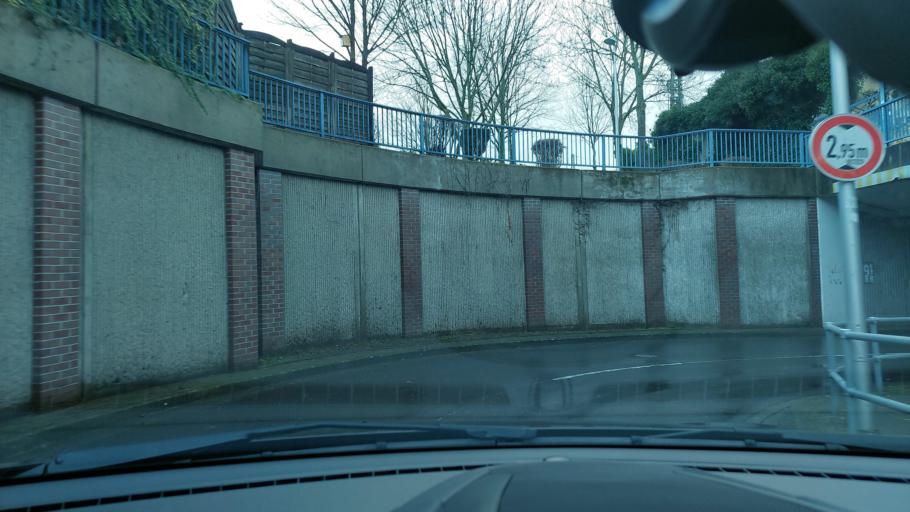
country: DE
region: North Rhine-Westphalia
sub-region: Regierungsbezirk Dusseldorf
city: Dormagen
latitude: 51.0994
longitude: 6.8146
